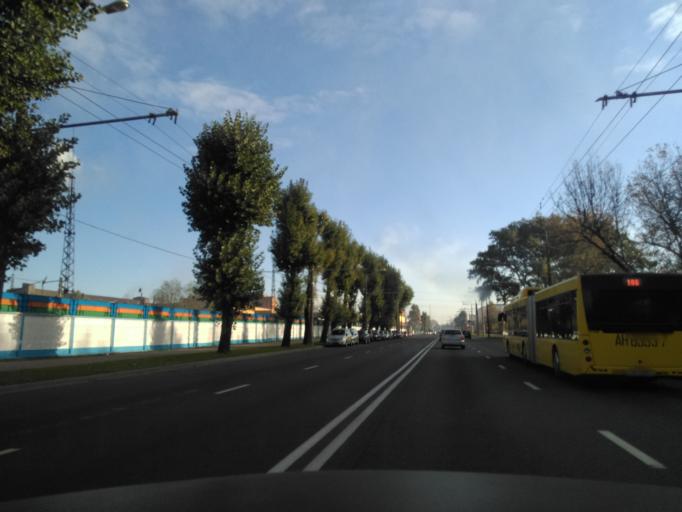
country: BY
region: Minsk
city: Minsk
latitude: 53.8874
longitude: 27.6271
